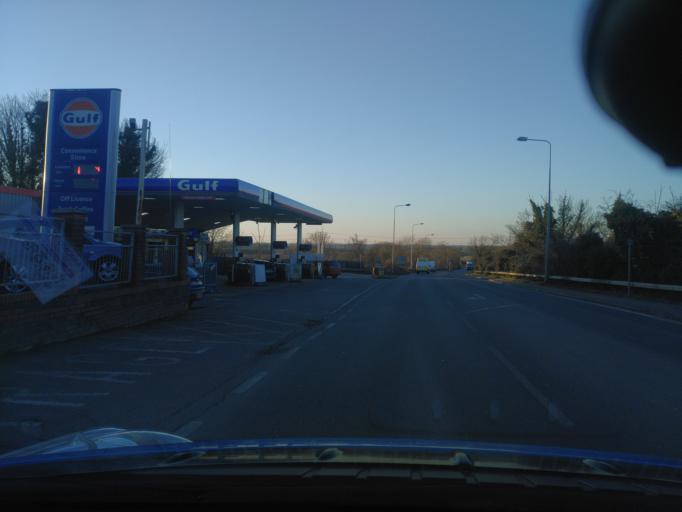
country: GB
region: England
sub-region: Central Bedfordshire
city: Houghton Regis
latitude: 51.9024
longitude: -0.5460
